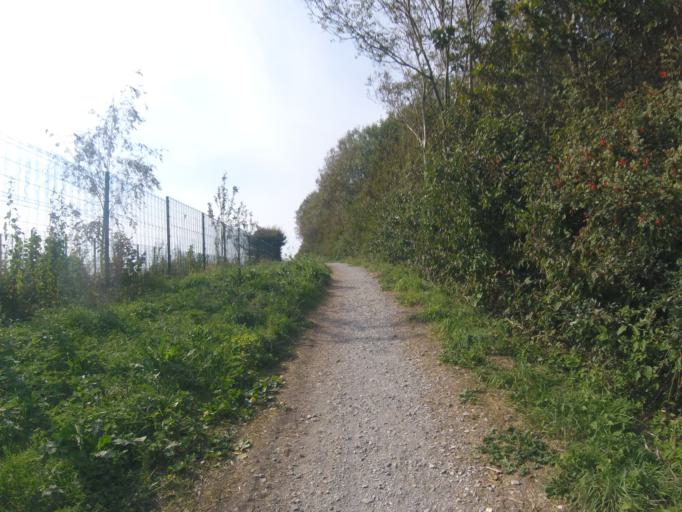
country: GB
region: England
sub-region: East Sussex
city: Portslade
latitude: 50.8545
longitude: -0.1922
